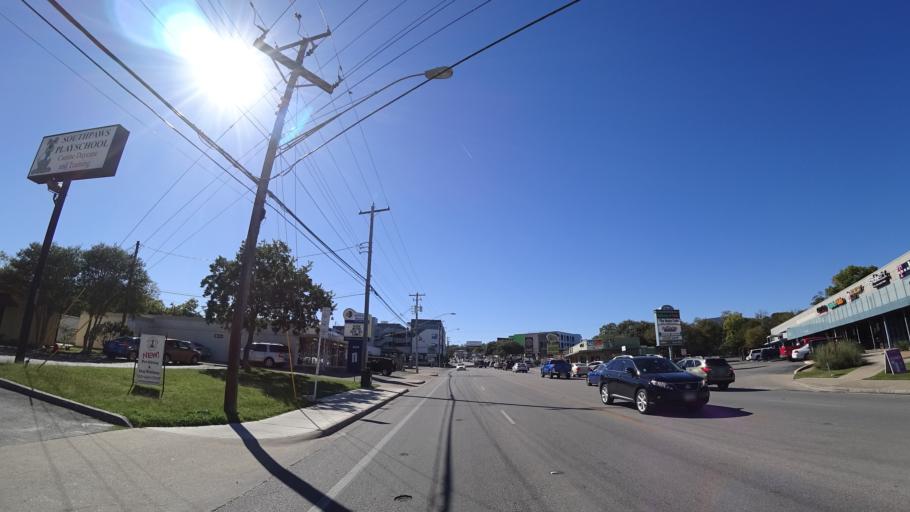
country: US
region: Texas
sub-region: Travis County
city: Rollingwood
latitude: 30.2474
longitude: -97.7741
